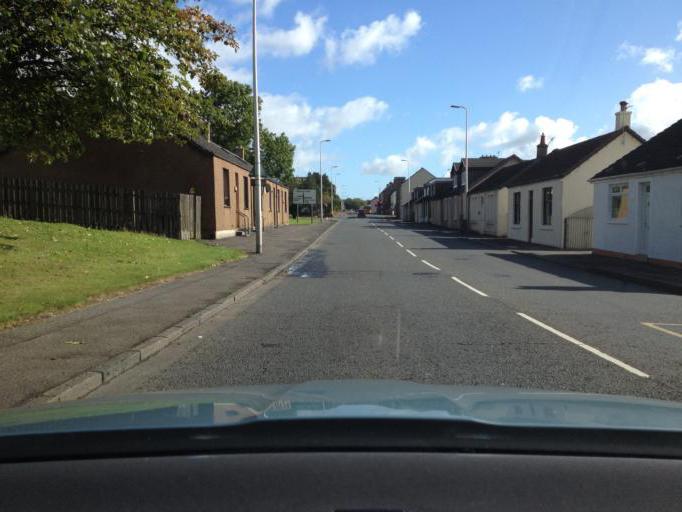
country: GB
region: Scotland
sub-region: West Lothian
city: Blackburn
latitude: 55.8711
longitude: -3.6262
